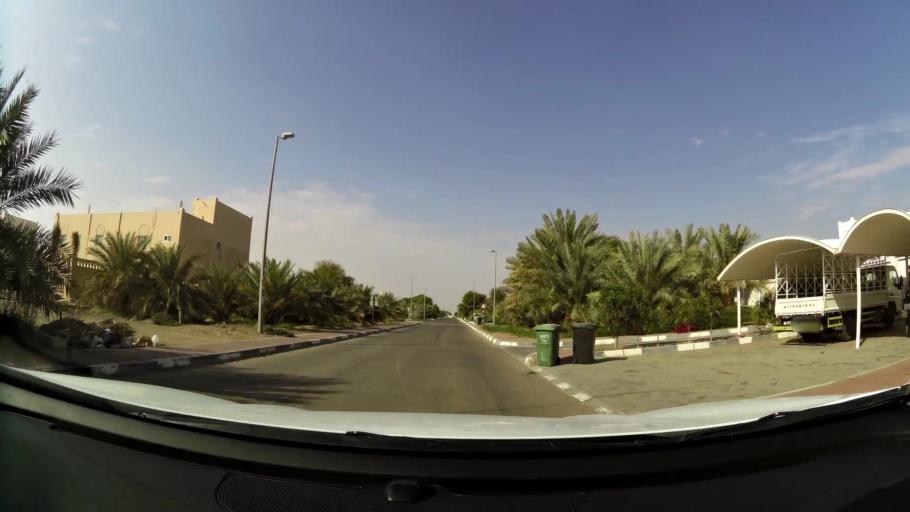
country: AE
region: Abu Dhabi
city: Al Ain
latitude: 24.0756
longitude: 55.8686
